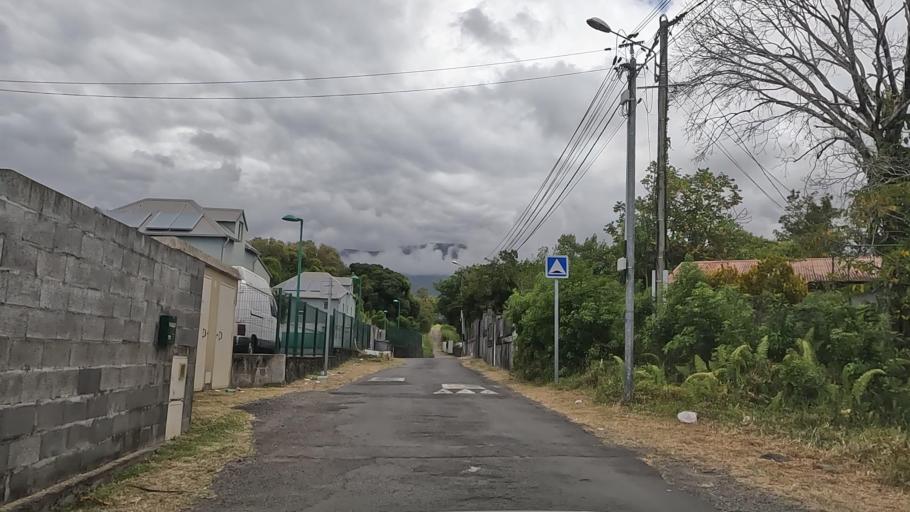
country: RE
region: Reunion
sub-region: Reunion
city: Saint-Benoit
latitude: -21.0921
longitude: 55.7448
